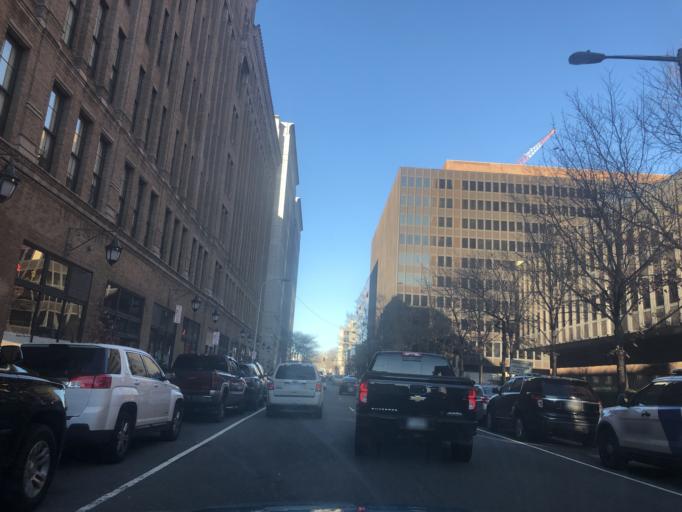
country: US
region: Pennsylvania
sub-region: Philadelphia County
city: Philadelphia
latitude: 39.9512
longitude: -75.1520
